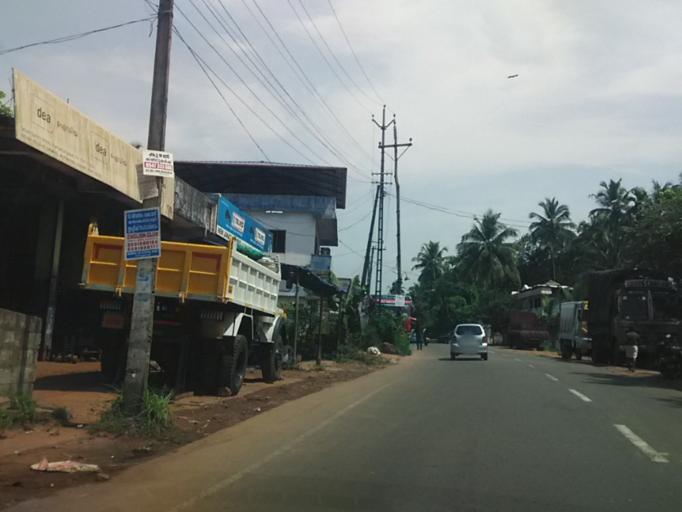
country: IN
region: Kerala
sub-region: Kozhikode
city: Kunnamangalam
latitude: 11.3150
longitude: 75.8844
